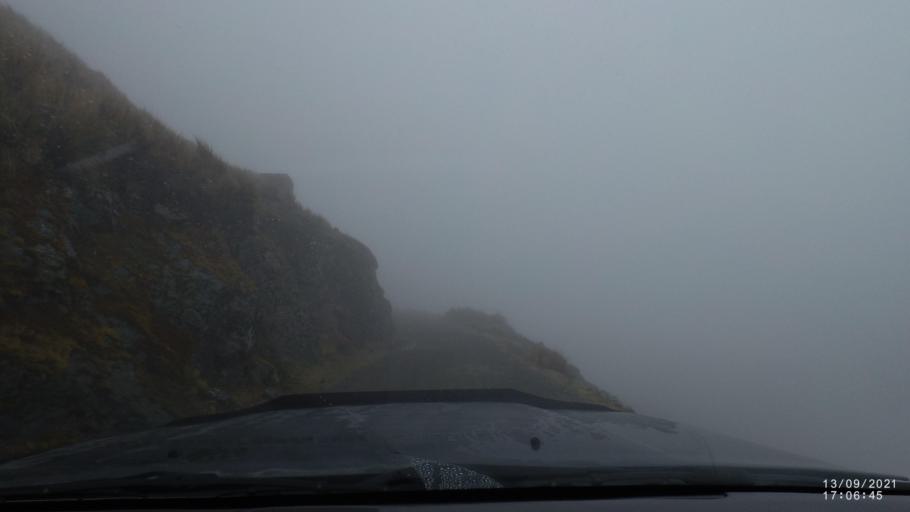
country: BO
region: Cochabamba
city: Colomi
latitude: -17.3274
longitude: -65.7220
